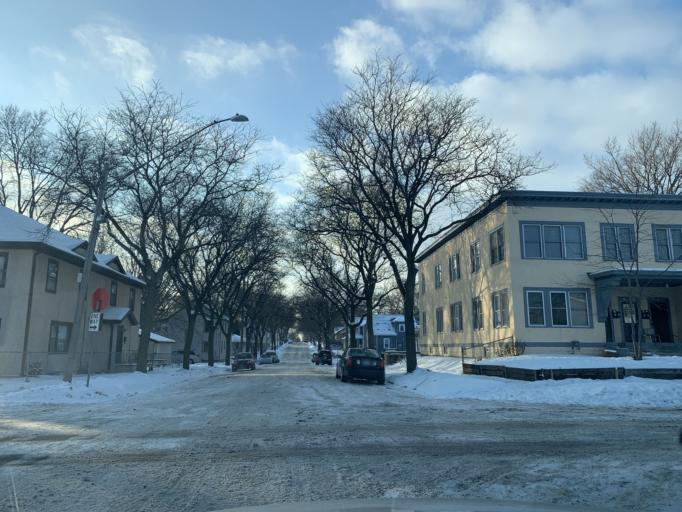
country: US
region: Minnesota
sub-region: Hennepin County
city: Minneapolis
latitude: 44.9861
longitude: -93.3031
